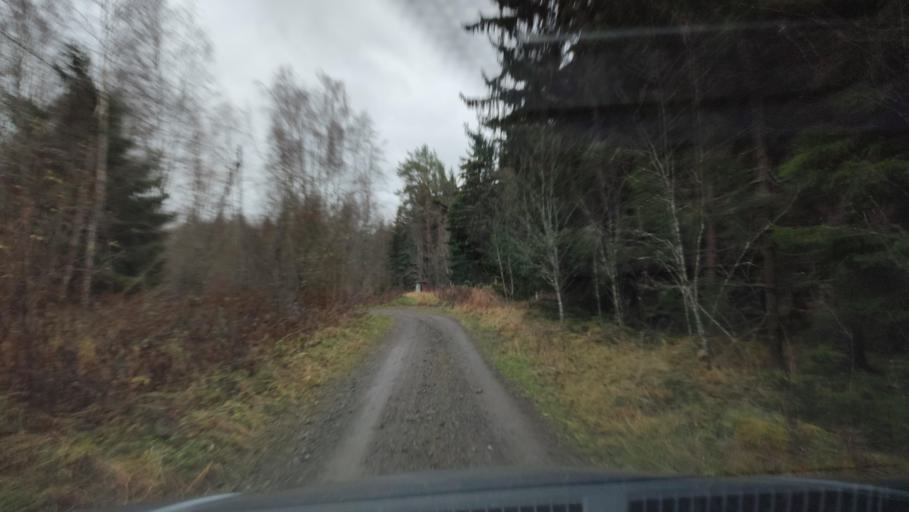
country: FI
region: Ostrobothnia
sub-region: Sydosterbotten
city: Kristinestad
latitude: 62.2772
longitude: 21.4135
